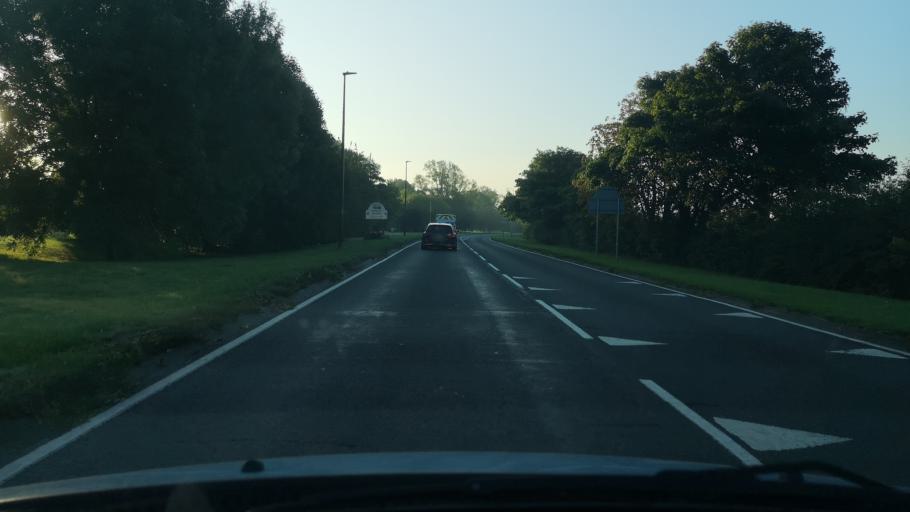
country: GB
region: England
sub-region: North Lincolnshire
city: Crowle
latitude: 53.5975
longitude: -0.8231
